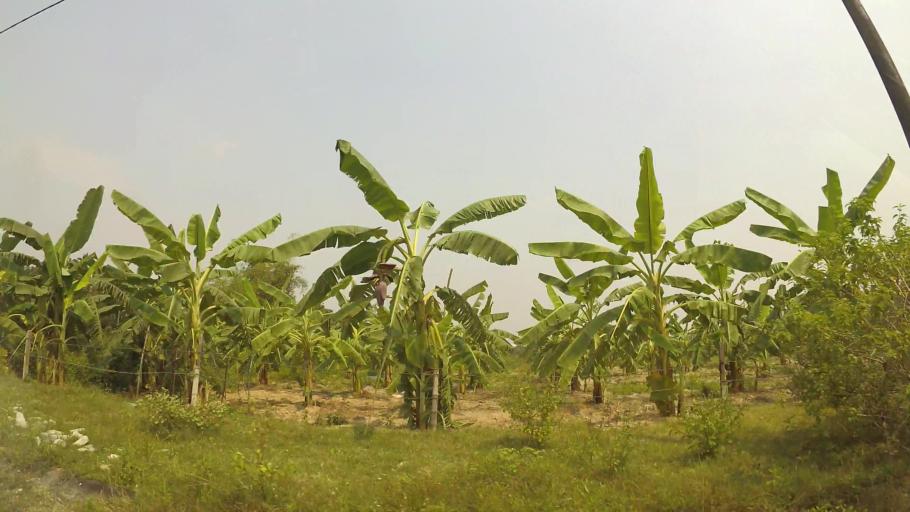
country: VN
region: Da Nang
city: Cam Le
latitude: 15.9860
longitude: 108.2107
